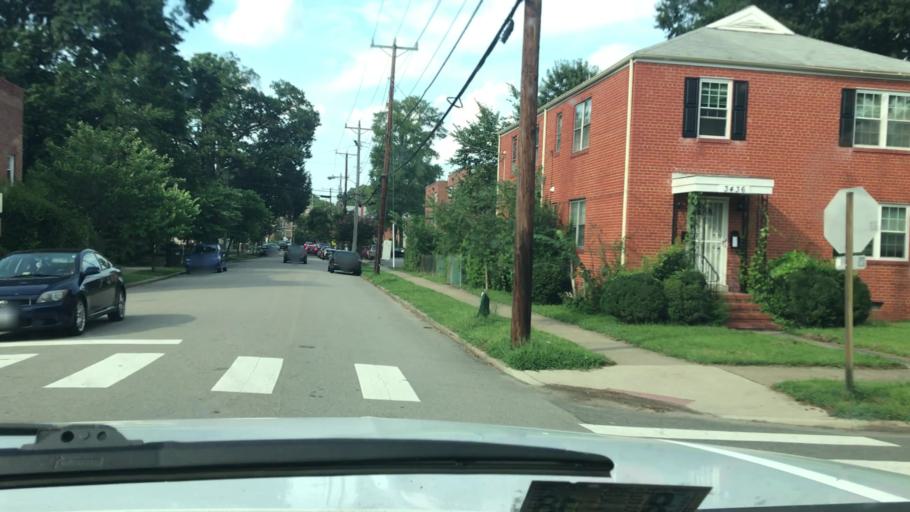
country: US
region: Virginia
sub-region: City of Richmond
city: Richmond
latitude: 37.5609
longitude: -77.4834
